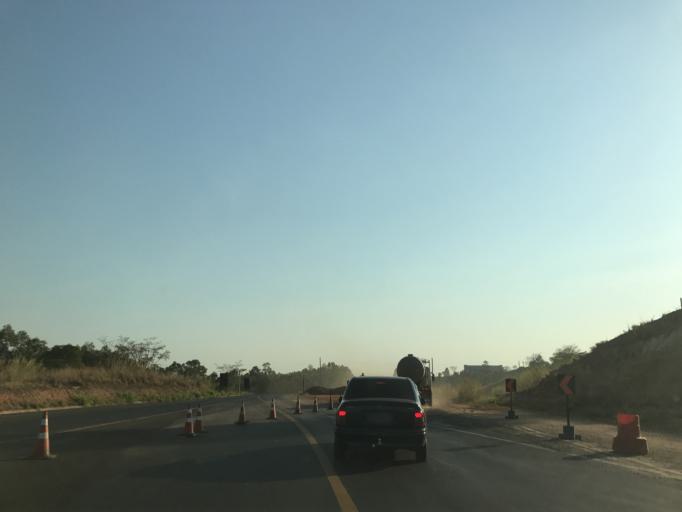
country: BR
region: Sao Paulo
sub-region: Marilia
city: Marilia
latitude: -22.1161
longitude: -49.9286
